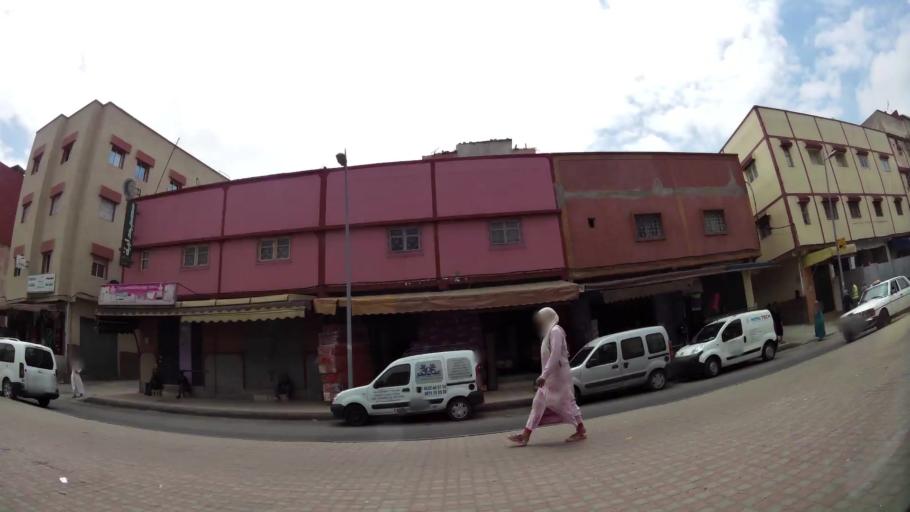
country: MA
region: Rabat-Sale-Zemmour-Zaer
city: Sale
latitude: 34.0542
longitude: -6.7801
